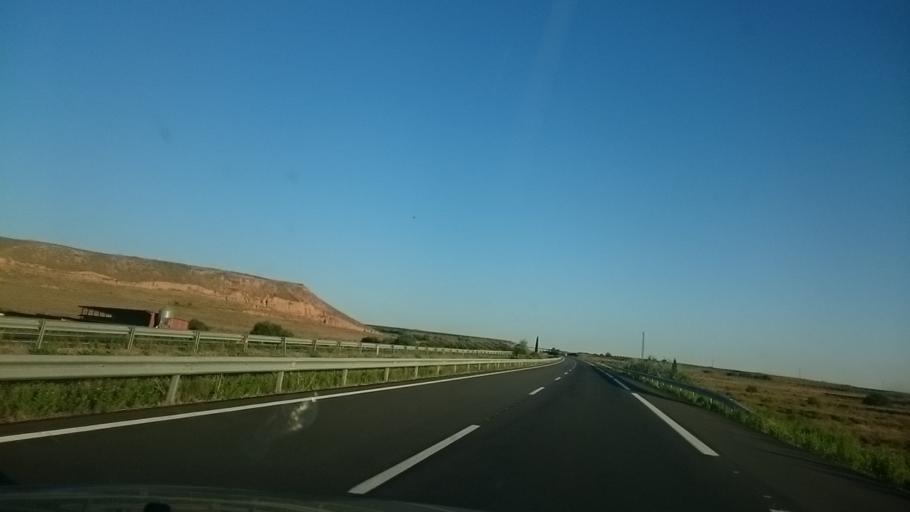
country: ES
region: La Rioja
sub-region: Provincia de La Rioja
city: Rincon de Soto
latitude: 42.2013
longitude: -1.8561
